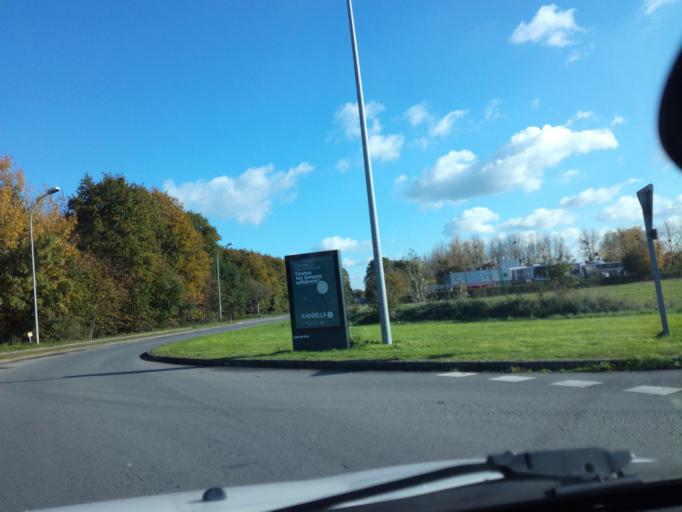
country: FR
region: Brittany
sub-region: Departement d'Ille-et-Vilaine
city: Mordelles
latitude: 48.0700
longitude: -1.8308
